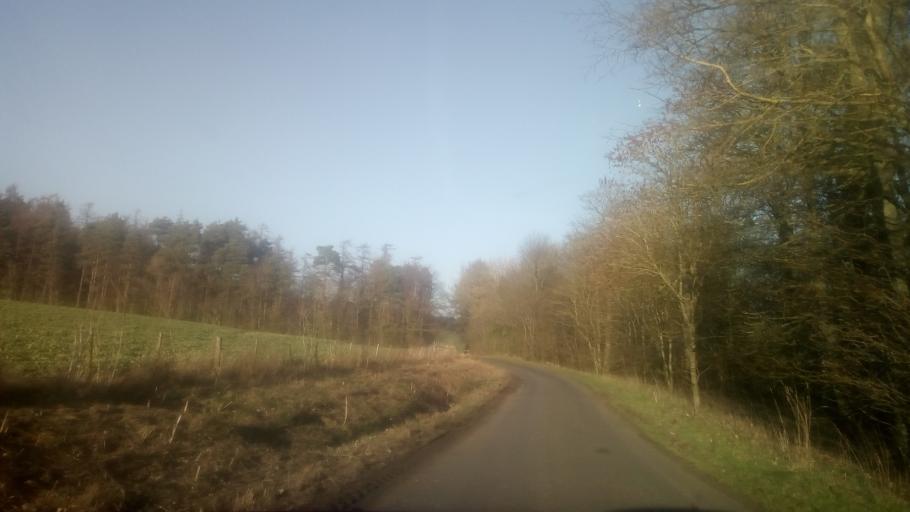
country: GB
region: Scotland
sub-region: The Scottish Borders
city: Saint Boswells
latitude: 55.4773
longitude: -2.6585
